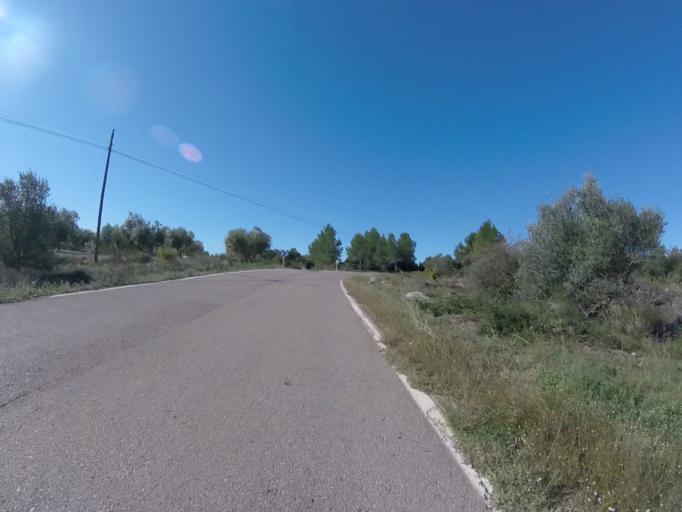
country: ES
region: Valencia
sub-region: Provincia de Castello
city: Chert/Xert
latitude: 40.4585
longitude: 0.1522
